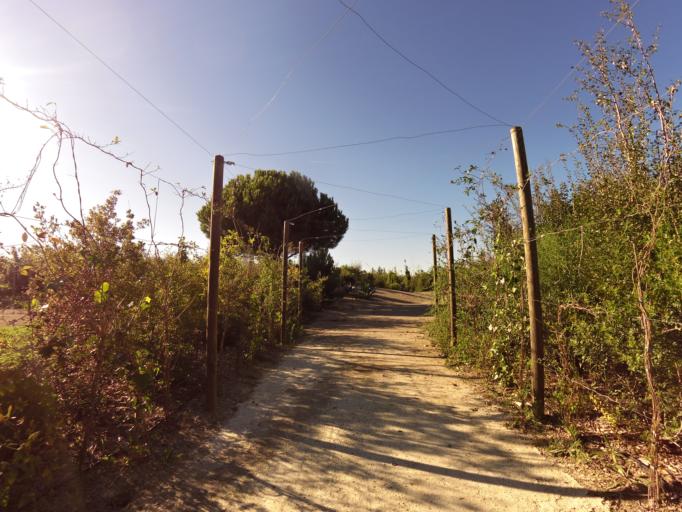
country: FR
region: Languedoc-Roussillon
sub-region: Departement de l'Herault
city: Lunel
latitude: 43.6632
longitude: 4.1326
